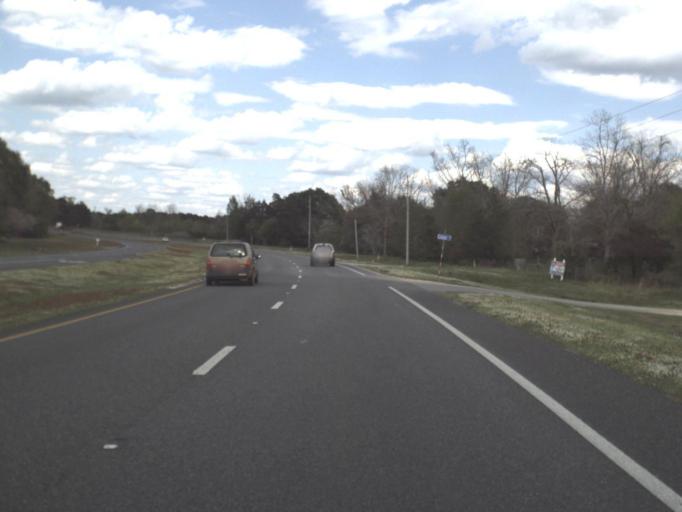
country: US
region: Florida
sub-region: Okaloosa County
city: Crestview
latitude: 30.8089
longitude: -86.5450
